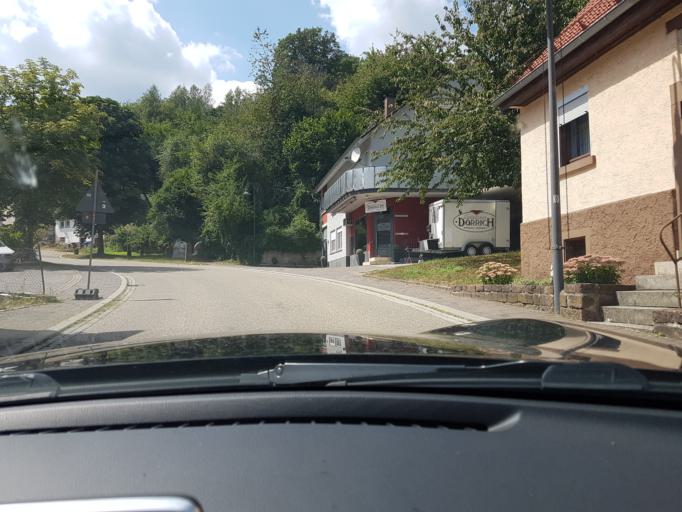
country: DE
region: Baden-Wuerttemberg
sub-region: Karlsruhe Region
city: Limbach
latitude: 49.4255
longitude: 9.2329
